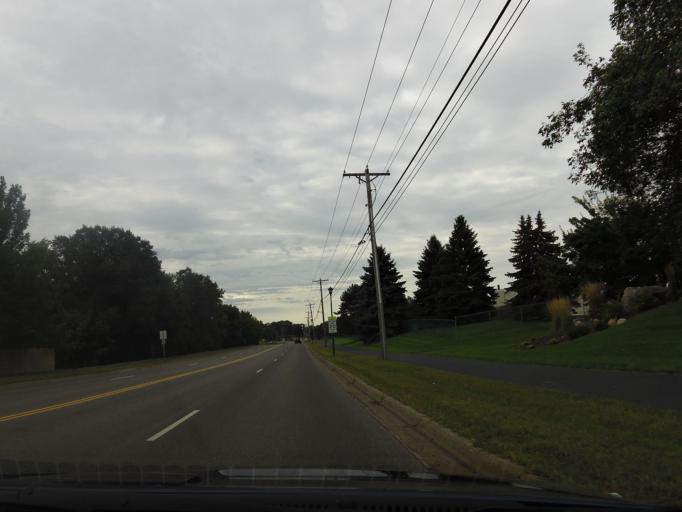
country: US
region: Minnesota
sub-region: Washington County
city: Cottage Grove
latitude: 44.8376
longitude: -92.9494
